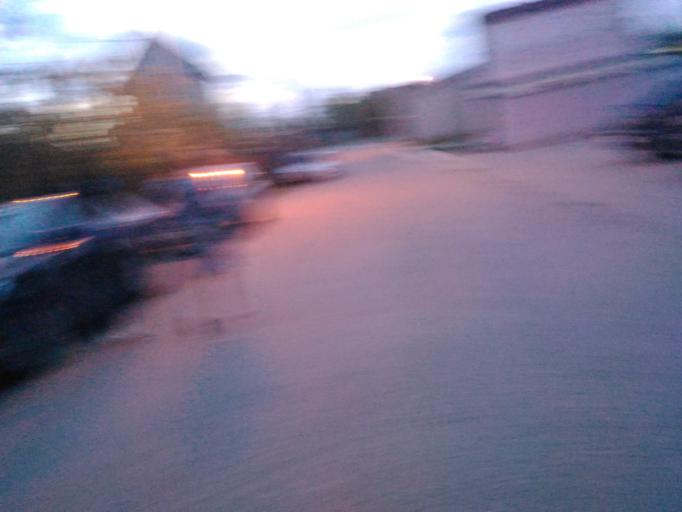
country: RU
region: Ulyanovsk
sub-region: Ulyanovskiy Rayon
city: Ulyanovsk
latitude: 54.2770
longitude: 48.3523
